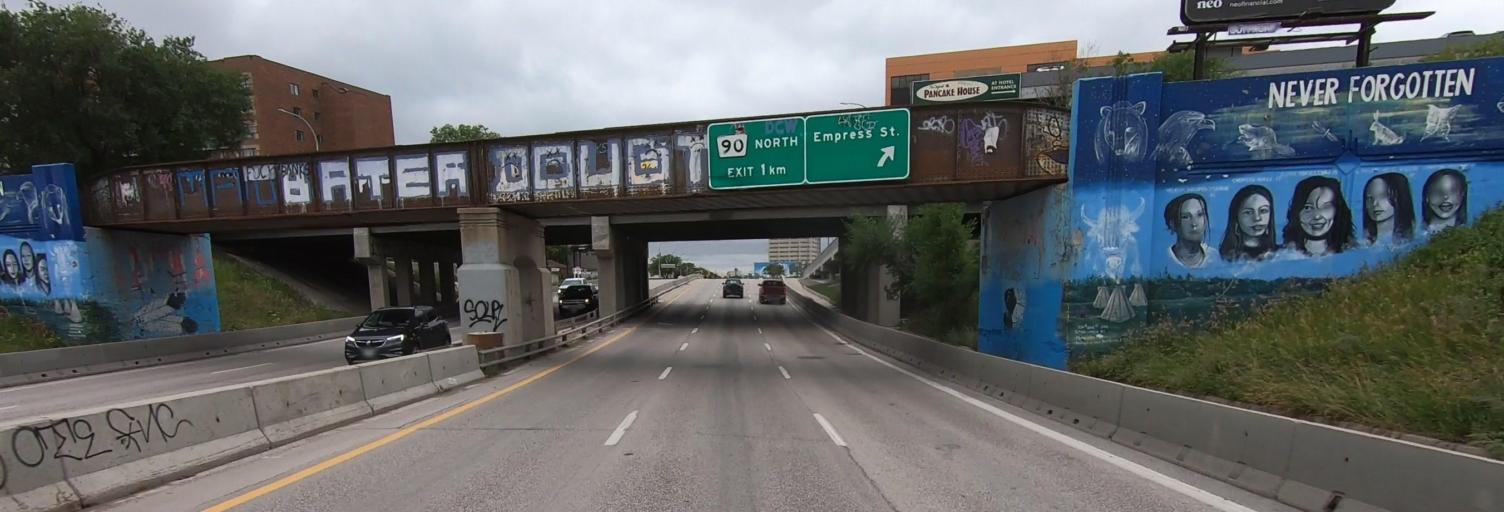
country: CA
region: Manitoba
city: Winnipeg
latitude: 49.8816
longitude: -97.1942
